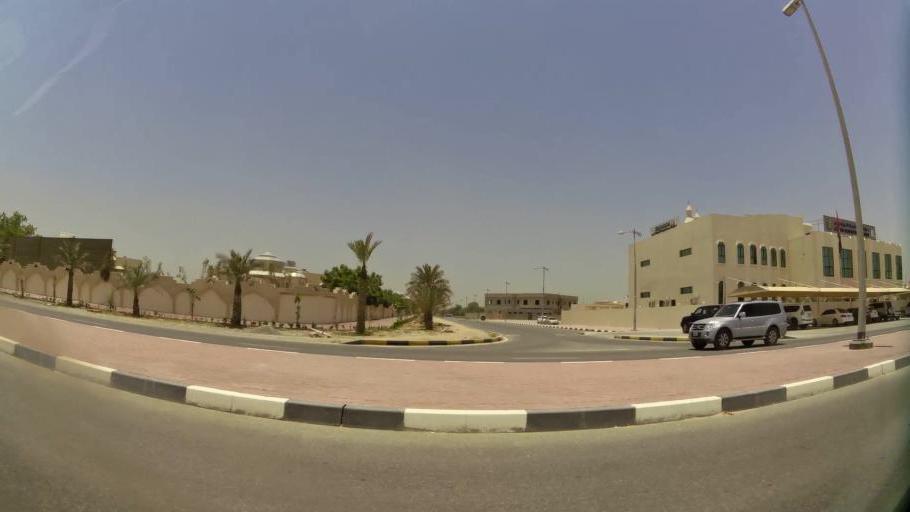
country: AE
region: Ajman
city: Ajman
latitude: 25.4108
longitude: 55.4866
